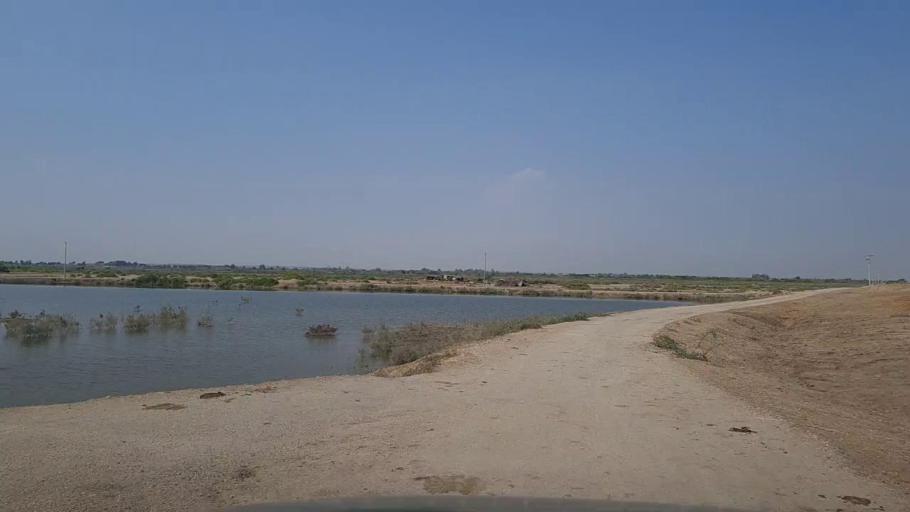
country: PK
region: Sindh
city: Thatta
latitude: 24.5725
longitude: 67.9164
